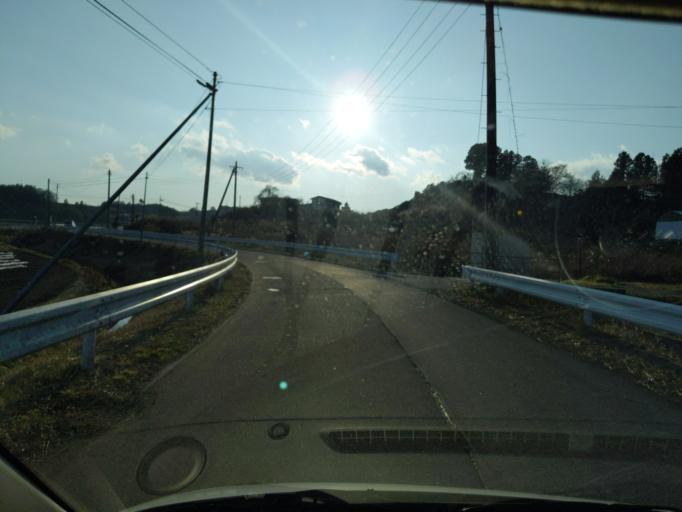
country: JP
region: Miyagi
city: Wakuya
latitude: 38.7053
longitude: 141.1235
